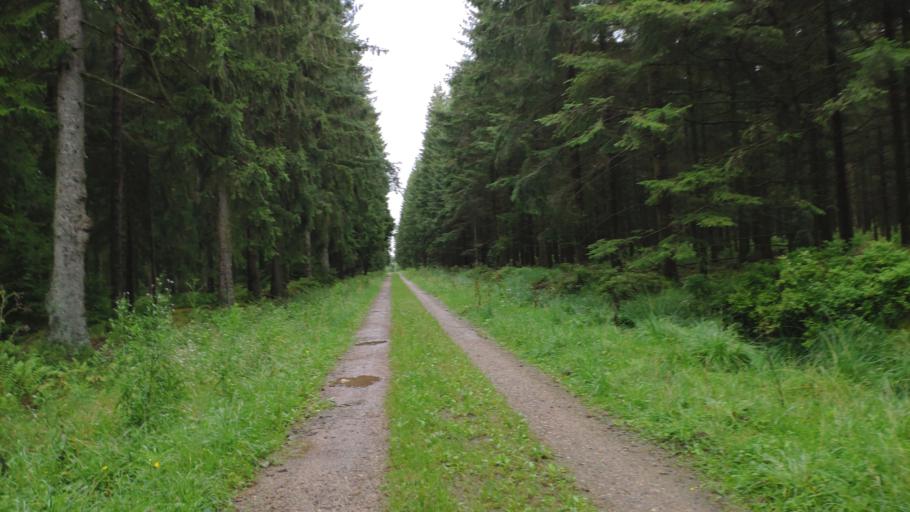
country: DE
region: North Rhine-Westphalia
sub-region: Regierungsbezirk Koln
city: Roetgen
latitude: 50.6353
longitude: 6.1682
